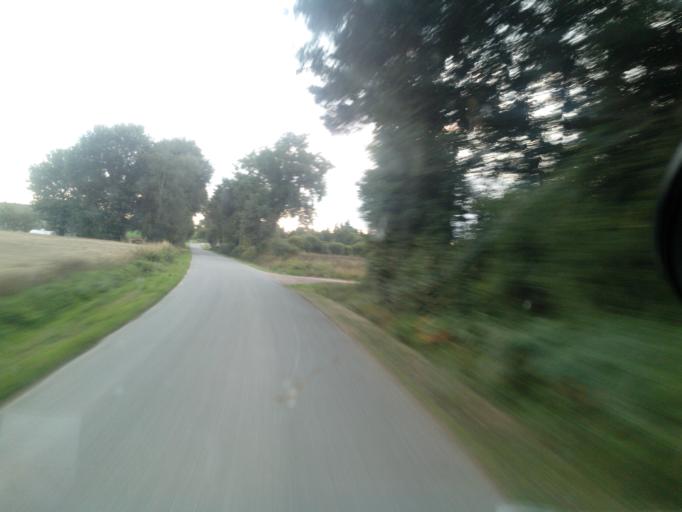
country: FR
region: Brittany
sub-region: Departement du Morbihan
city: Guegon
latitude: 47.9277
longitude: -2.5755
